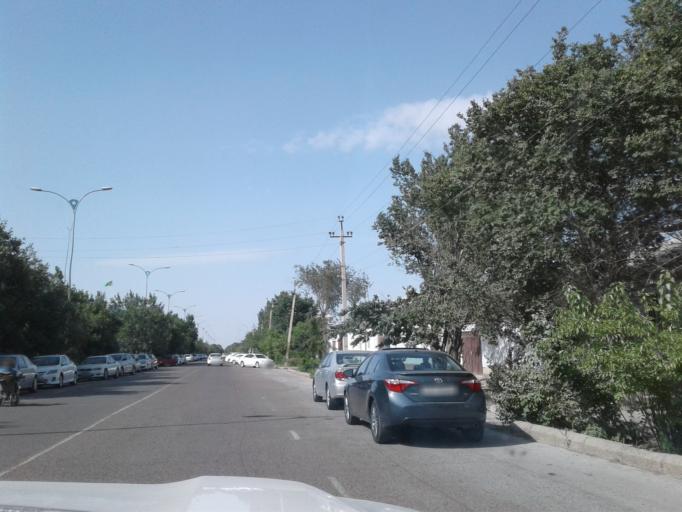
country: TM
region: Dasoguz
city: Dasoguz
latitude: 41.8309
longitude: 59.9609
